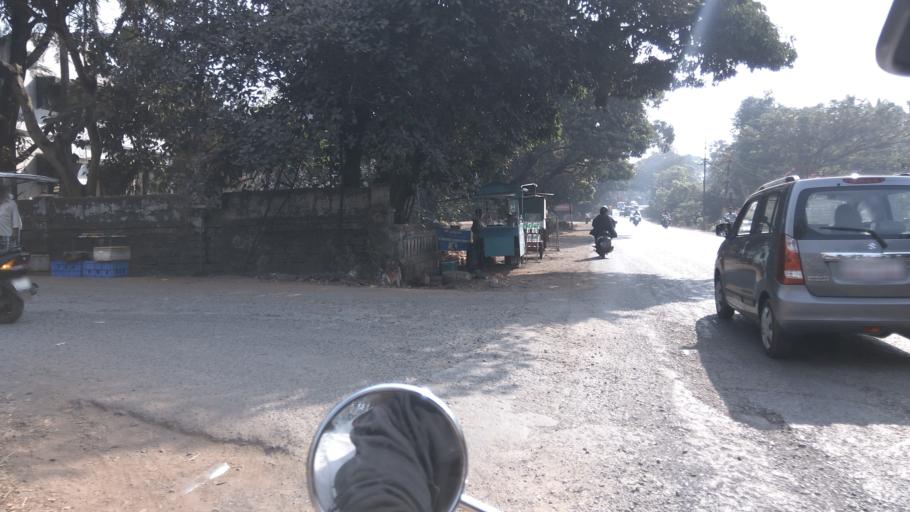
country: IN
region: Goa
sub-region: North Goa
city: Jua
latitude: 15.4965
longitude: 73.9317
